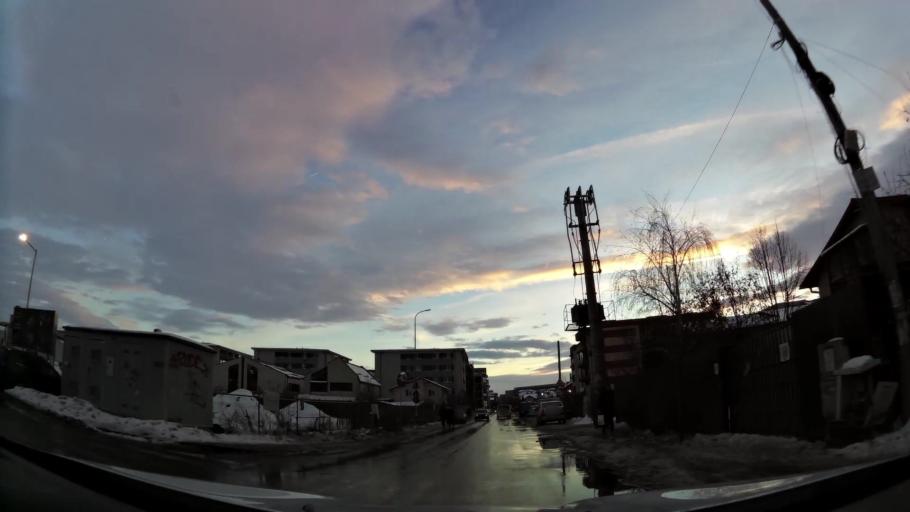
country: RO
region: Ilfov
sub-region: Comuna Popesti-Leordeni
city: Popesti-Leordeni
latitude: 44.3687
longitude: 26.1521
